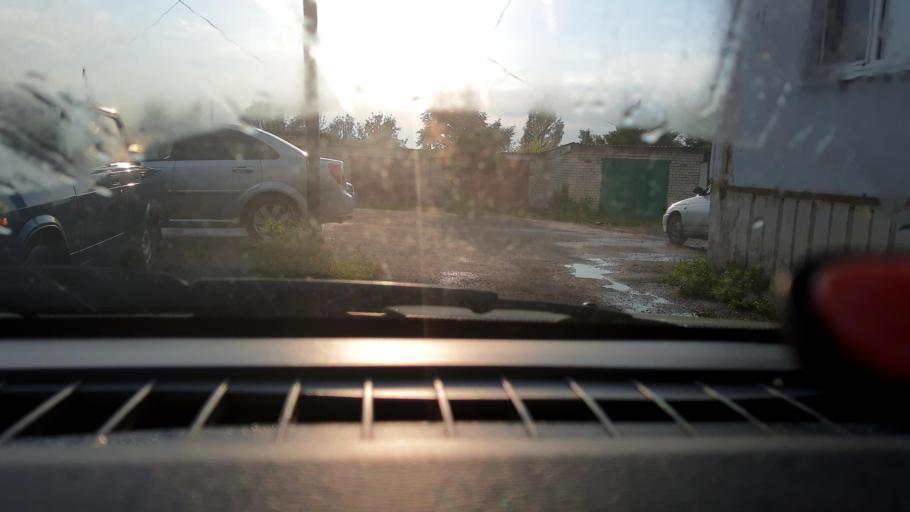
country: RU
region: Nizjnij Novgorod
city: Lukoyanov
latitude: 55.0449
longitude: 44.4938
